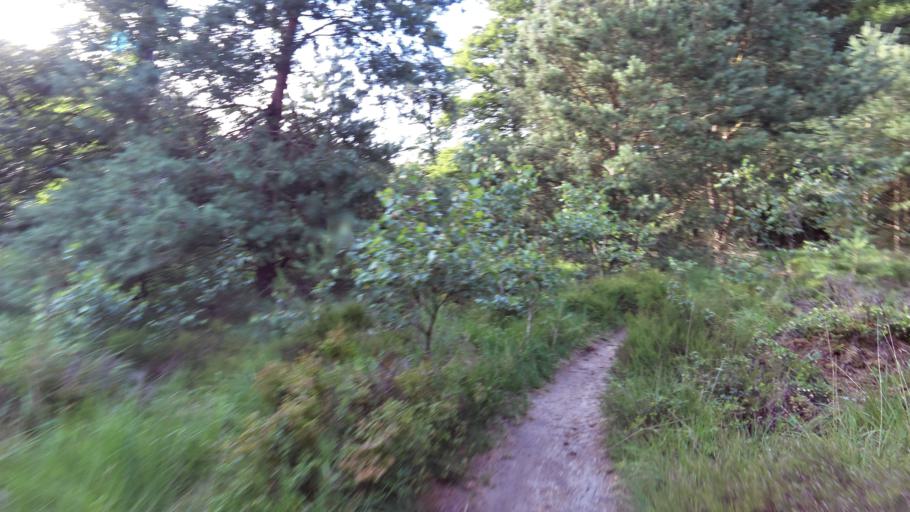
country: NL
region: Gelderland
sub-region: Gemeente Apeldoorn
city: Uddel
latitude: 52.2178
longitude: 5.8502
